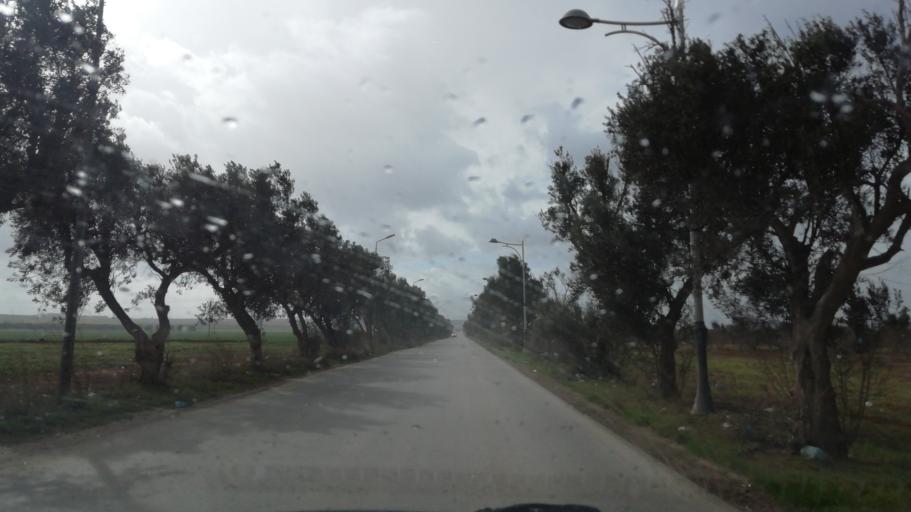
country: DZ
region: Oran
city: Sidi ech Chahmi
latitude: 35.6533
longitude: -0.5224
